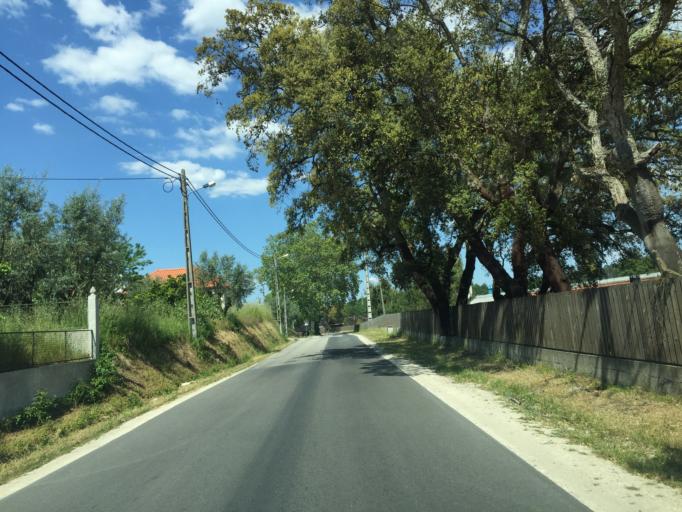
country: PT
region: Santarem
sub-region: Ourem
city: Ourem
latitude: 39.7159
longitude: -8.5205
